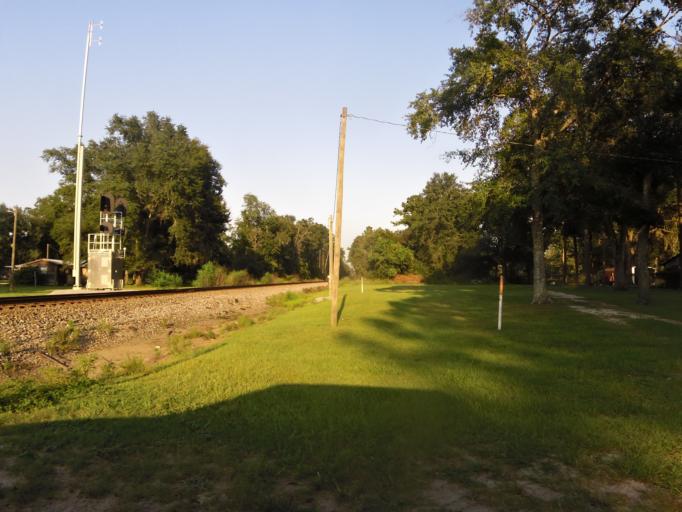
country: US
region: Florida
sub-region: Nassau County
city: Hilliard
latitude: 30.5211
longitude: -82.0350
